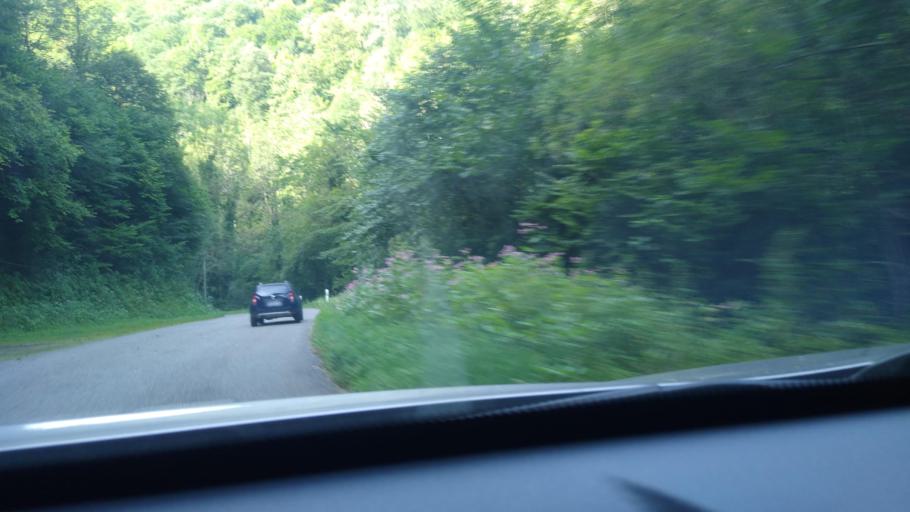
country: FR
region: Midi-Pyrenees
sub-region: Departement de l'Ariege
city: Saint-Girons
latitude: 42.8152
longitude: 1.1963
